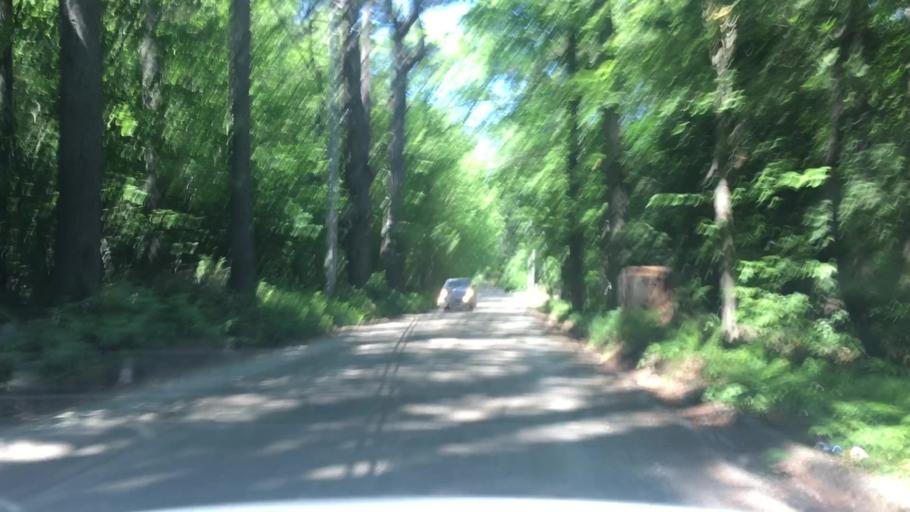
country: US
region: New Hampshire
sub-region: Merrimack County
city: Hopkinton
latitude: 43.2288
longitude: -71.6663
